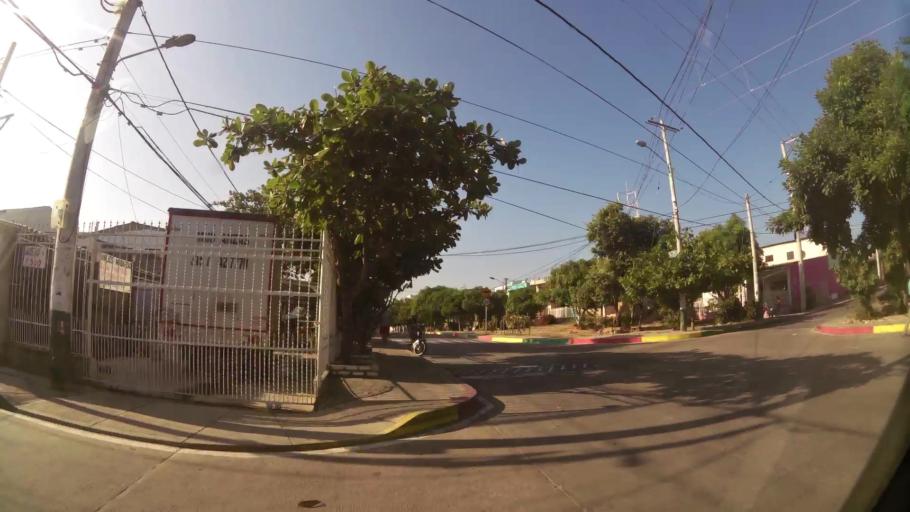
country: CO
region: Bolivar
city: Cartagena
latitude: 10.4034
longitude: -75.5000
